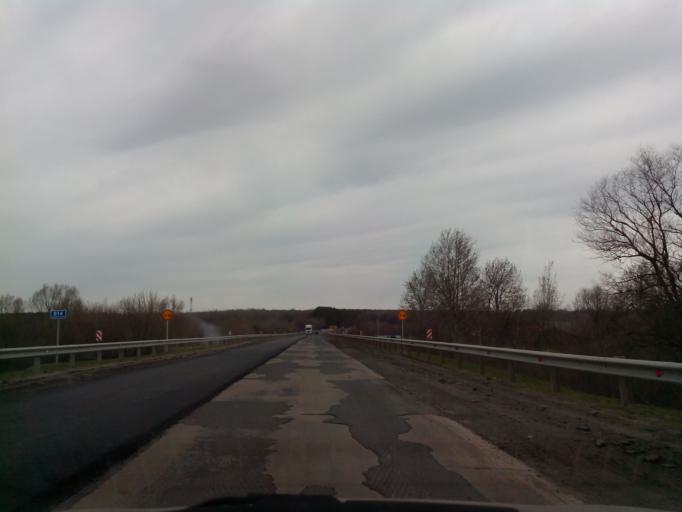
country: RU
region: Tambov
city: Znamenka
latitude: 52.5273
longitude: 41.3592
